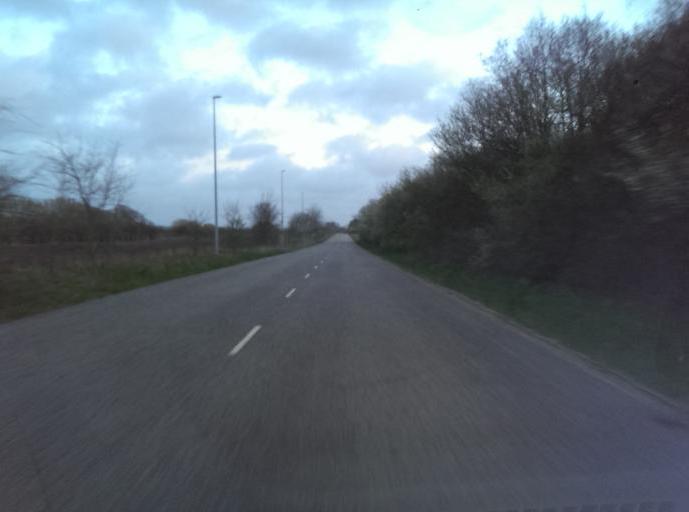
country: DK
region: South Denmark
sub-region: Esbjerg Kommune
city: Esbjerg
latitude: 55.4992
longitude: 8.5014
